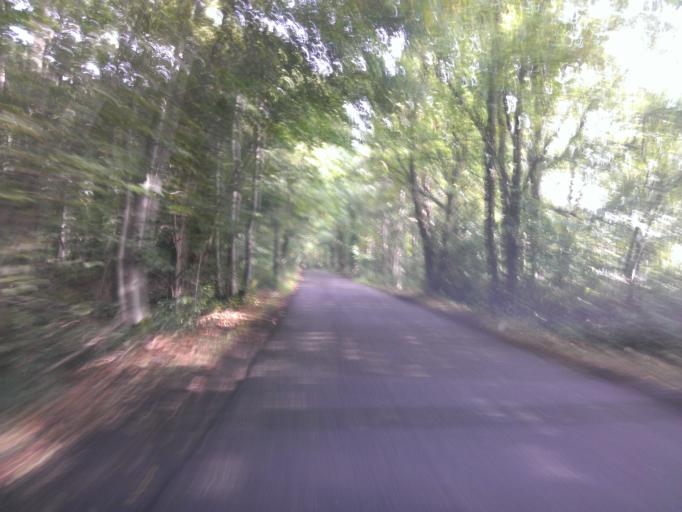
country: GB
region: England
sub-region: Essex
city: Little Clacton
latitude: 51.8353
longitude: 1.1043
